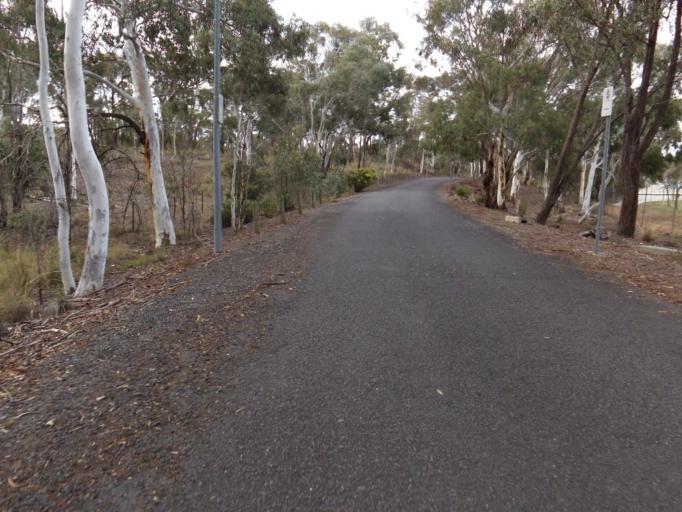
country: AU
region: Australian Capital Territory
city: Kaleen
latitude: -35.2505
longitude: 149.0986
